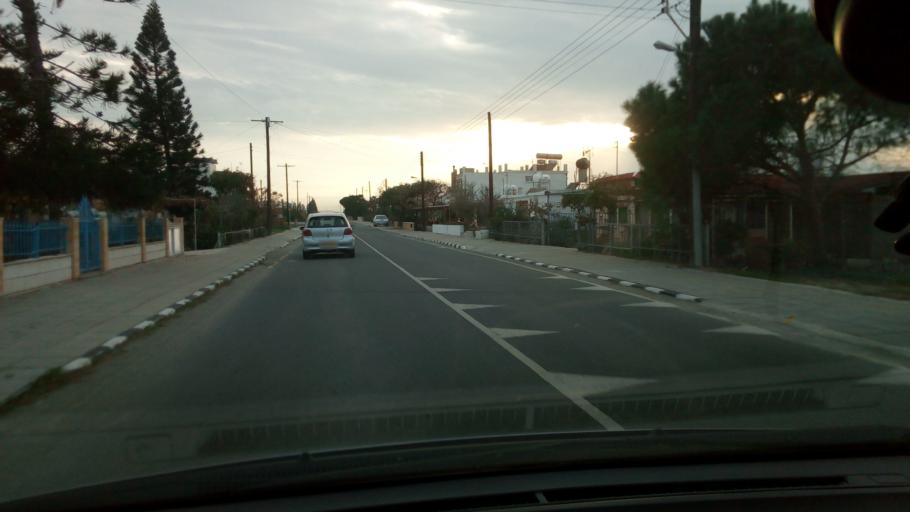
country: CY
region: Pafos
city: Polis
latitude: 35.1087
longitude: 32.5062
